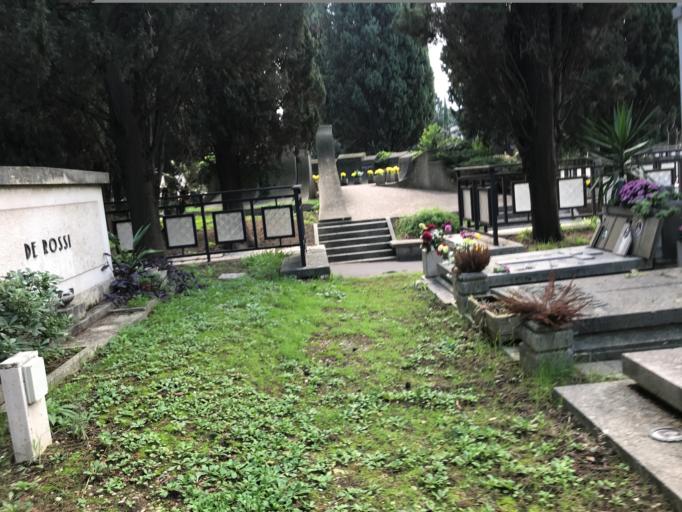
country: IT
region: Latium
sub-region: Citta metropolitana di Roma Capitale
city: Rome
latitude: 41.9075
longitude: 12.5309
